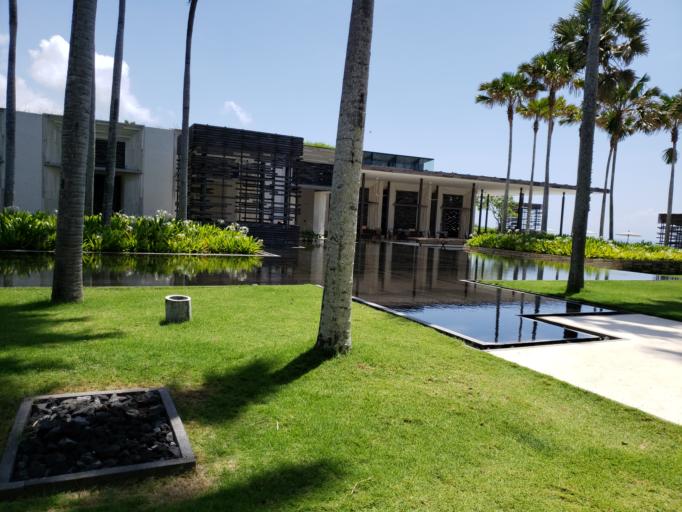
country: ID
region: Bali
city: Kangin
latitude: -8.8461
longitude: 115.1372
